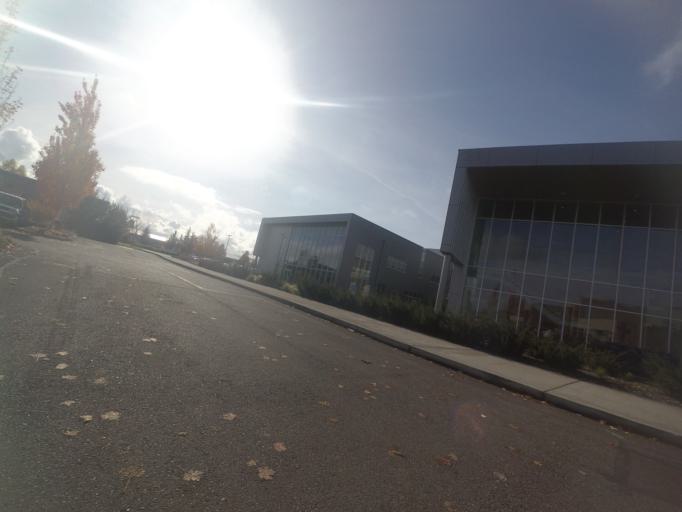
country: US
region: Washington
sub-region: Pierce County
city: Lakewood
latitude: 47.1748
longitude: -122.4978
